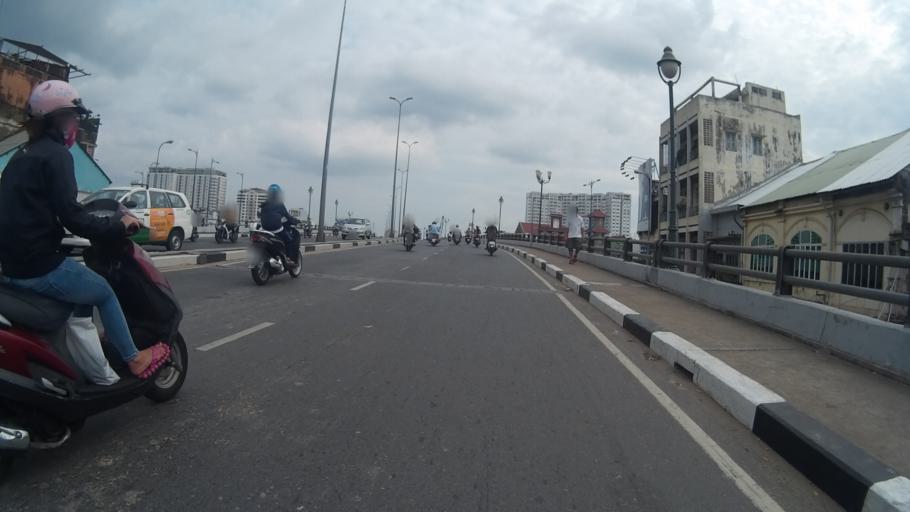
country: VN
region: Ho Chi Minh City
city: Quan Bon
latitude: 10.7644
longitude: 106.6975
